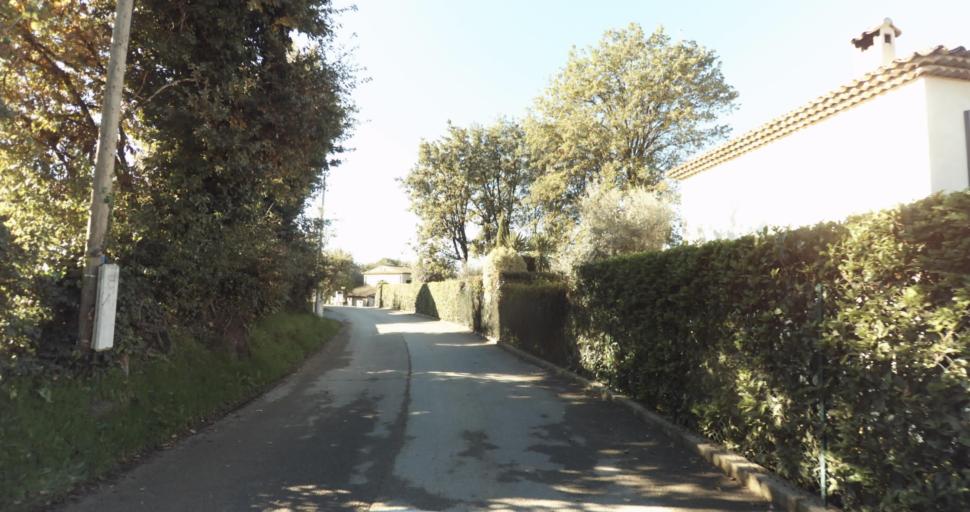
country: FR
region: Provence-Alpes-Cote d'Azur
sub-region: Departement des Alpes-Maritimes
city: Vence
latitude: 43.7150
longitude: 7.0860
